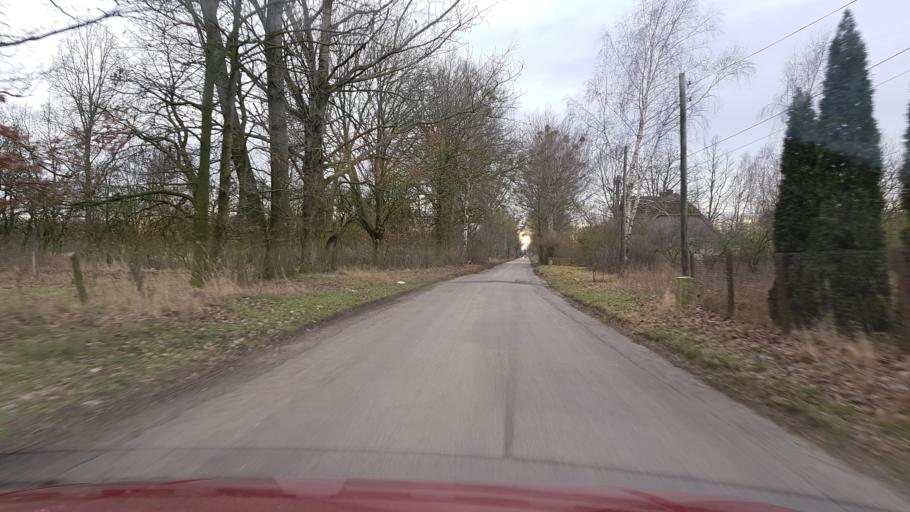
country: PL
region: West Pomeranian Voivodeship
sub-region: Powiat policki
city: Police
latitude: 53.5770
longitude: 14.5221
